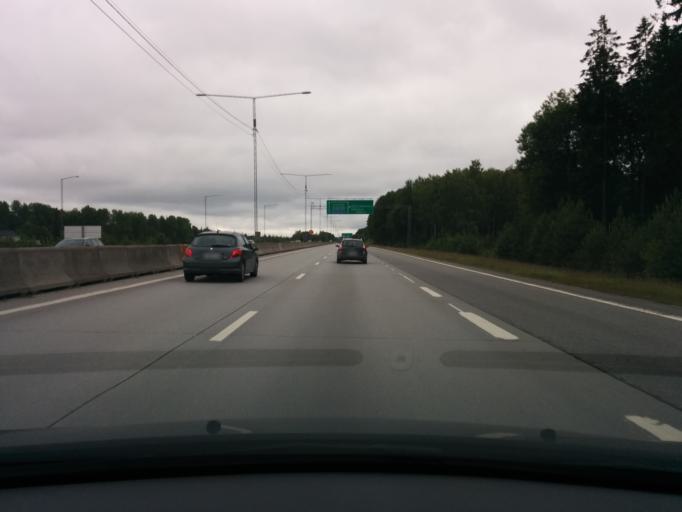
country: SE
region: Stockholm
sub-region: Sigtuna Kommun
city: Rosersberg
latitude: 59.6276
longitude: 17.9198
